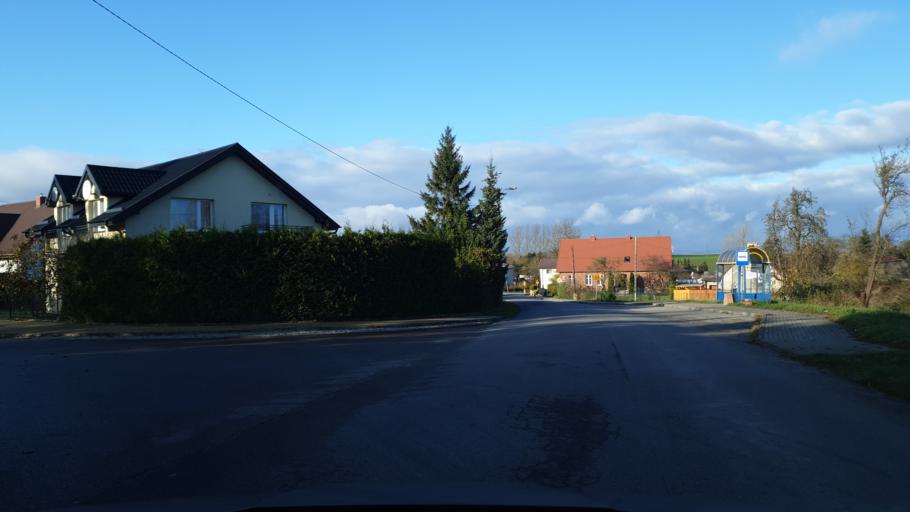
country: PL
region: Pomeranian Voivodeship
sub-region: Powiat pucki
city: Krokowa
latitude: 54.7848
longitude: 18.1988
